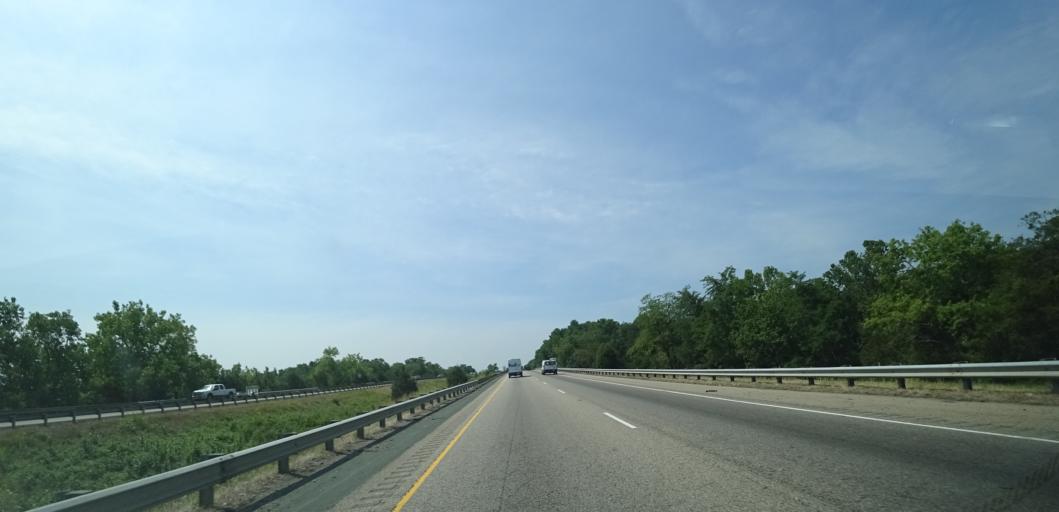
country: US
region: Virginia
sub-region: Augusta County
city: Verona
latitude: 38.2020
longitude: -78.9946
